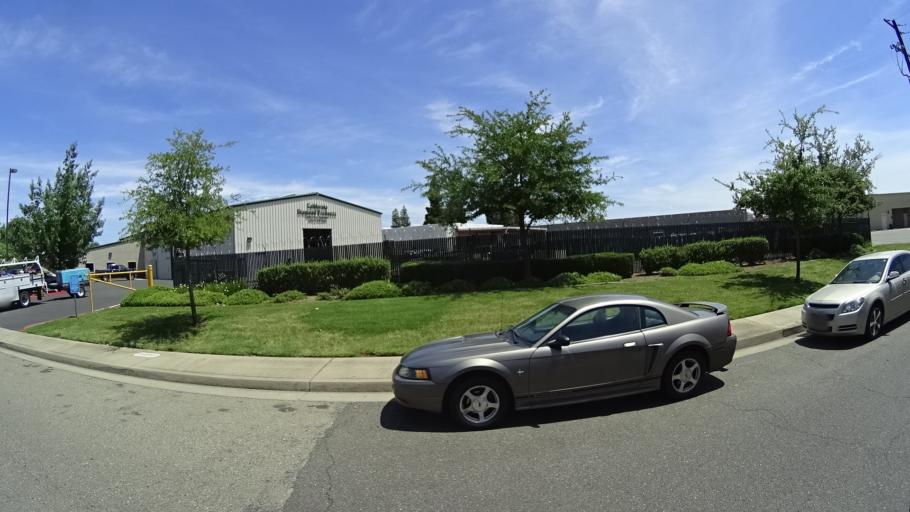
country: US
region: California
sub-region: Sacramento County
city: Florin
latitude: 38.5441
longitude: -121.4134
